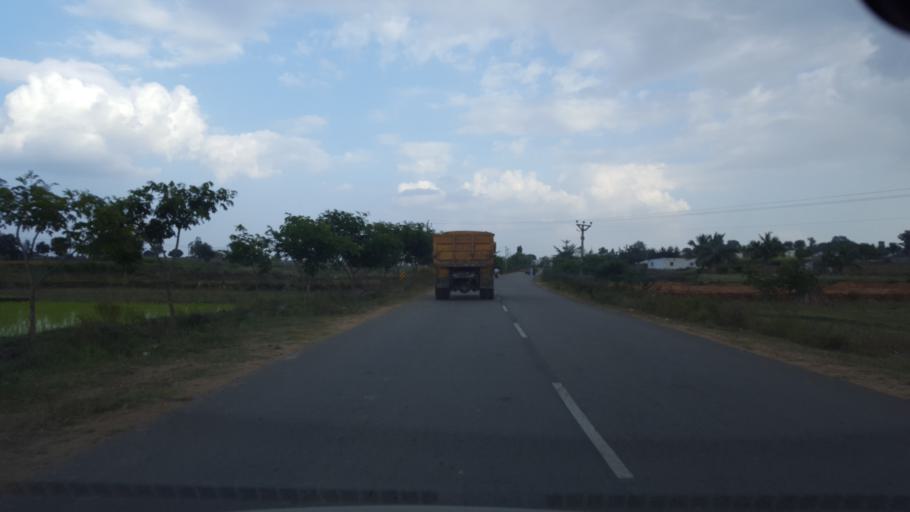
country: IN
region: Telangana
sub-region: Mahbubnagar
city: Mahbubnagar
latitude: 16.7611
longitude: 77.9536
